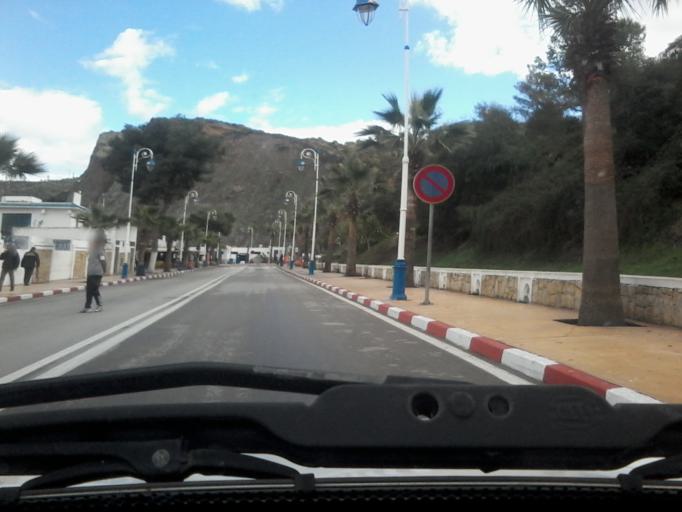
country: MA
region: Tanger-Tetouan
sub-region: Tetouan
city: Martil
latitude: 35.6815
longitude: -5.3136
